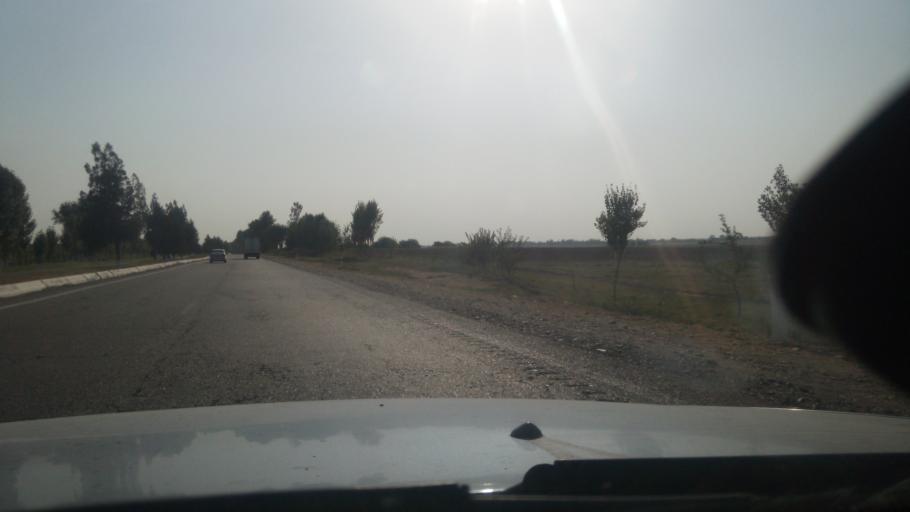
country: UZ
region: Toshkent
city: Zafar
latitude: 41.0047
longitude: 68.8282
